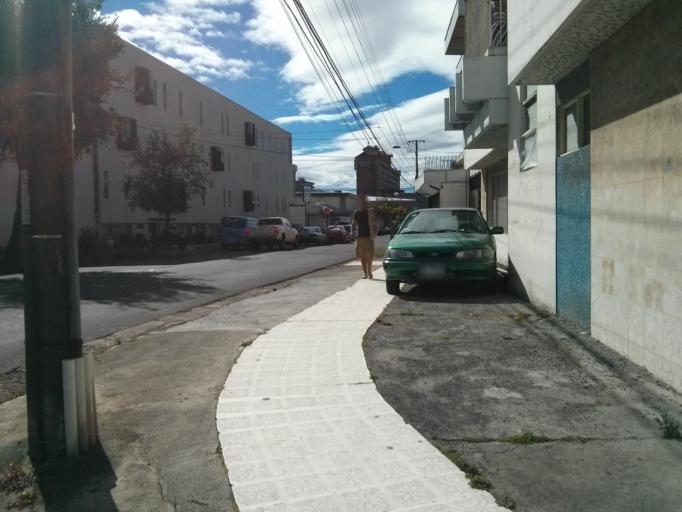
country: CR
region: San Jose
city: San Jose
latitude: 9.9396
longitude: -84.0959
